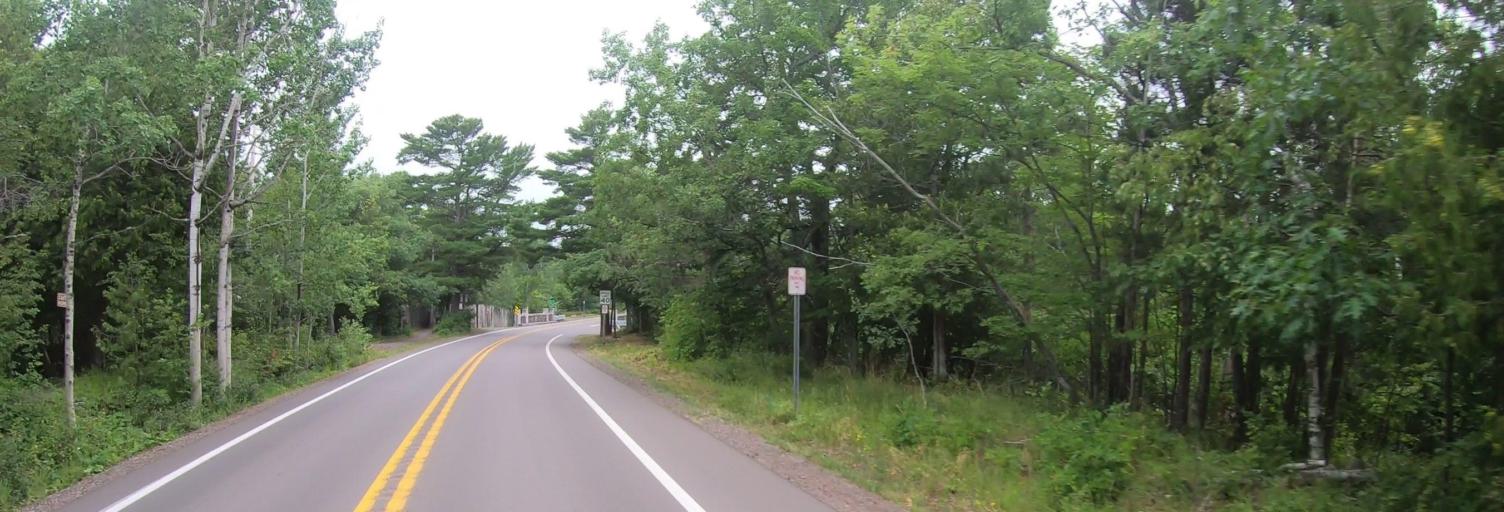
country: US
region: Michigan
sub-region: Keweenaw County
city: Eagle River
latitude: 47.4671
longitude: -87.8654
